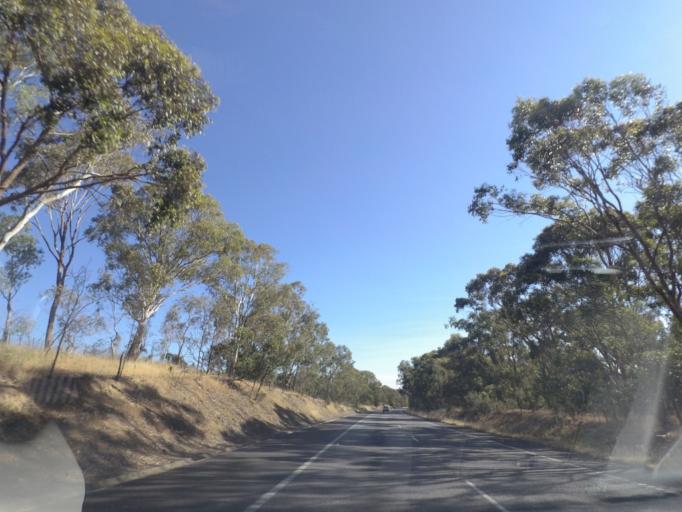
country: AU
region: Victoria
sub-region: Murrindindi
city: Kinglake West
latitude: -37.1699
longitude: 145.0767
